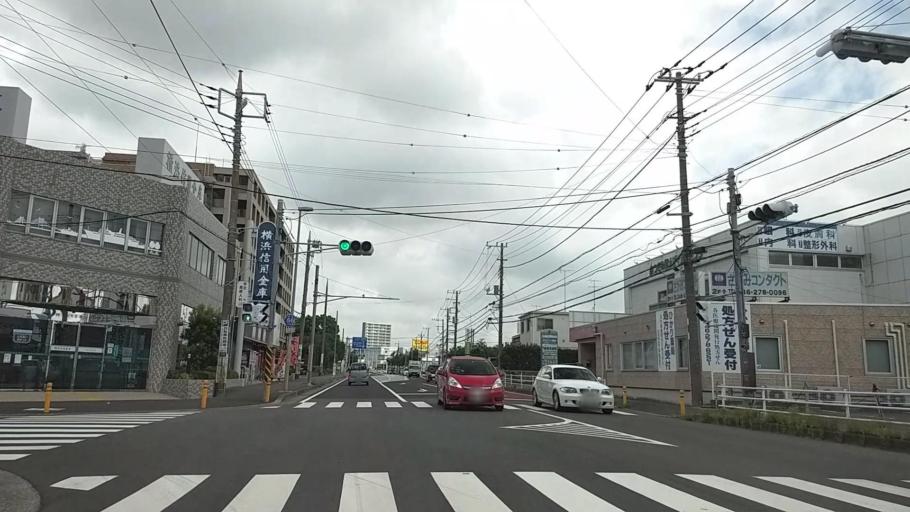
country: JP
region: Tokyo
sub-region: Machida-shi
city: Machida
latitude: 35.5119
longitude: 139.4590
